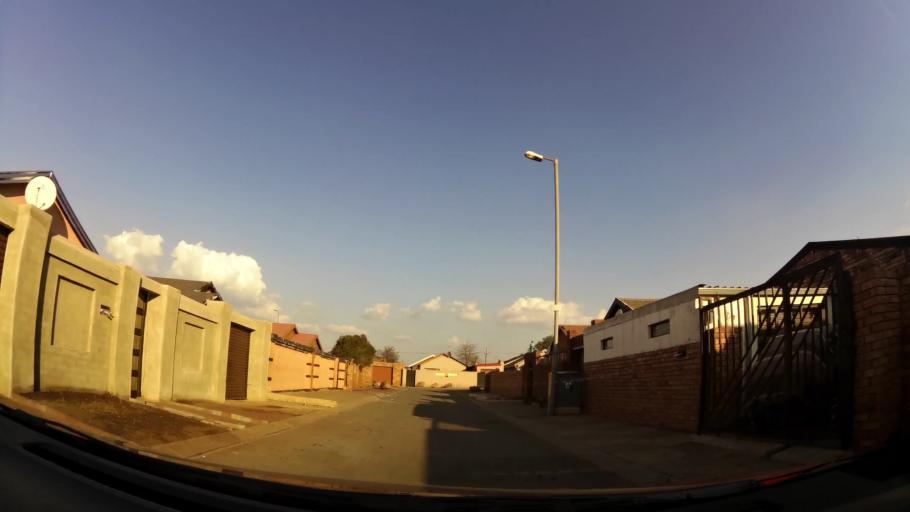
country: ZA
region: Gauteng
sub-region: City of Johannesburg Metropolitan Municipality
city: Soweto
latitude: -26.2288
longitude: 27.8565
